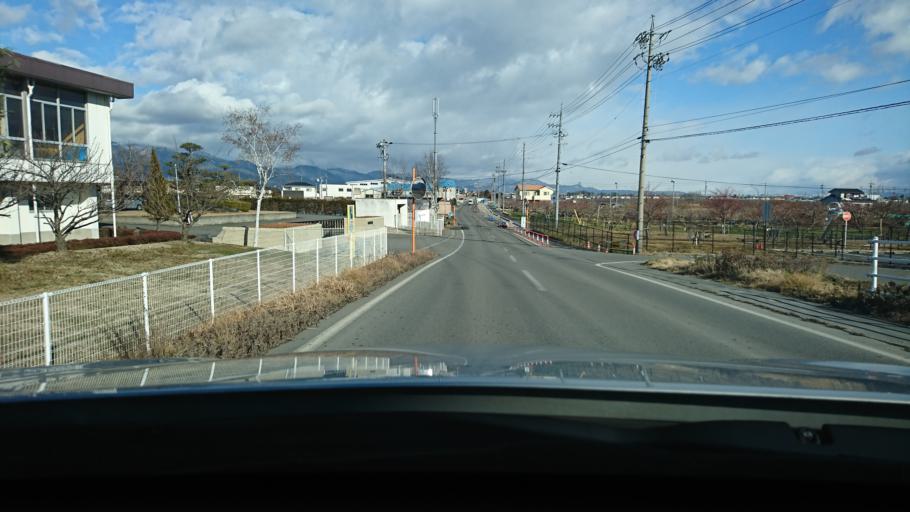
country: JP
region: Nagano
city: Nagano-shi
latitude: 36.5707
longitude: 138.1756
